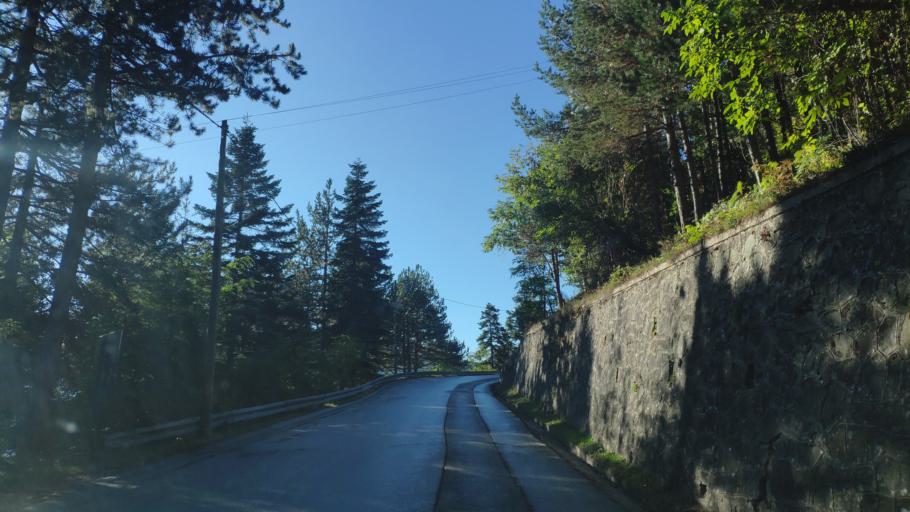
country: GR
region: Epirus
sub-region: Nomos Ioanninon
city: Metsovo
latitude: 39.7752
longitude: 21.1790
